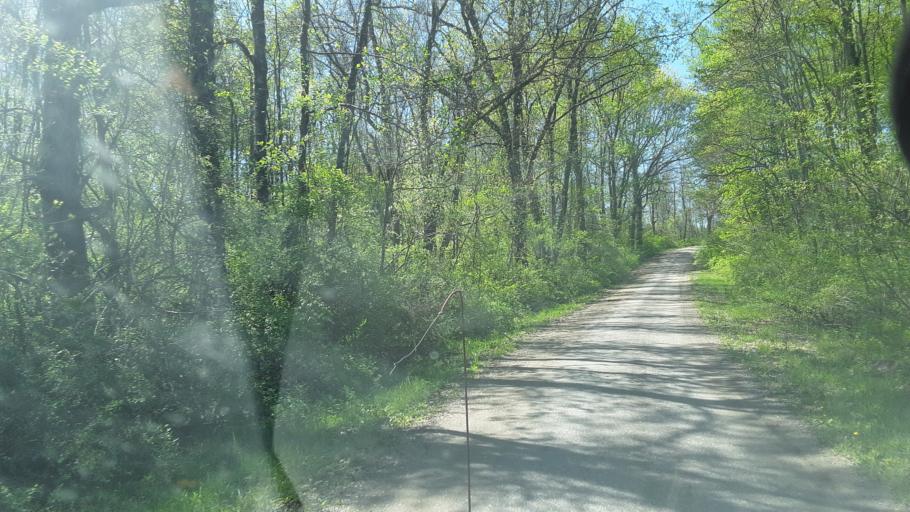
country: US
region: Ohio
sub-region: Noble County
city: Caldwell
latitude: 39.7683
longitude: -81.6162
